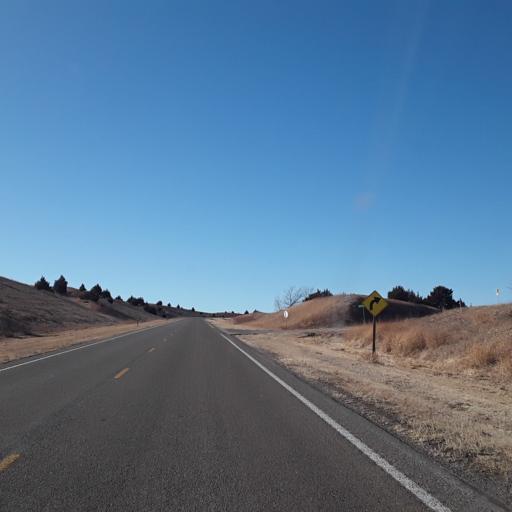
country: US
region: Nebraska
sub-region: Frontier County
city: Stockville
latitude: 40.6321
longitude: -100.5776
